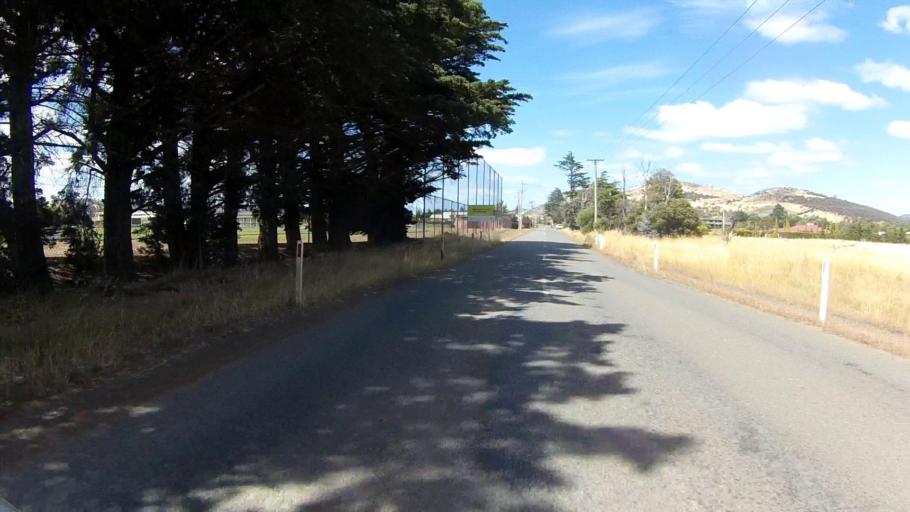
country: AU
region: Tasmania
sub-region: Clarence
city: Cambridge
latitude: -42.7295
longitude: 147.4359
